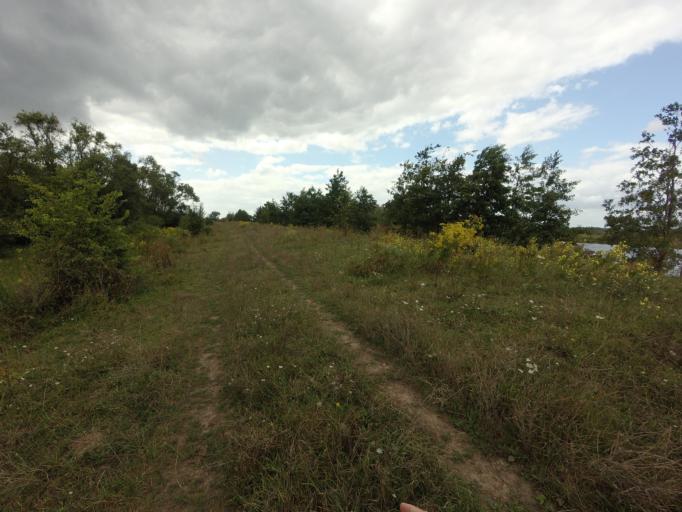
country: NL
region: Limburg
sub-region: Gemeente Maasgouw
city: Maasbracht
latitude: 51.1490
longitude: 5.8632
